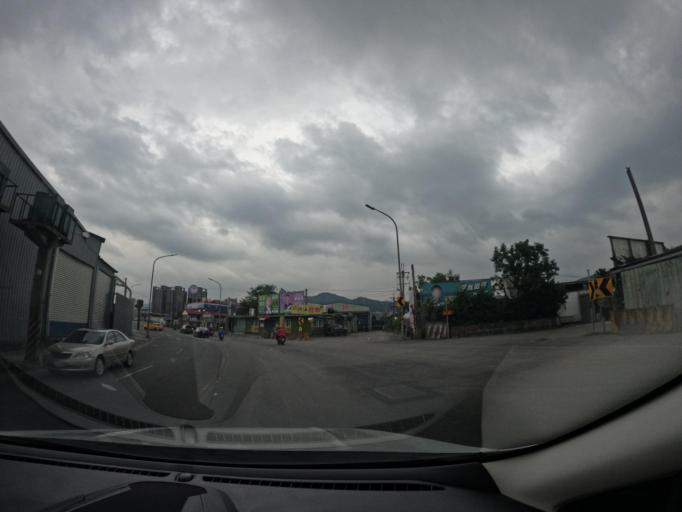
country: TW
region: Taipei
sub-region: Taipei
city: Banqiao
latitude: 24.9602
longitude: 121.4074
